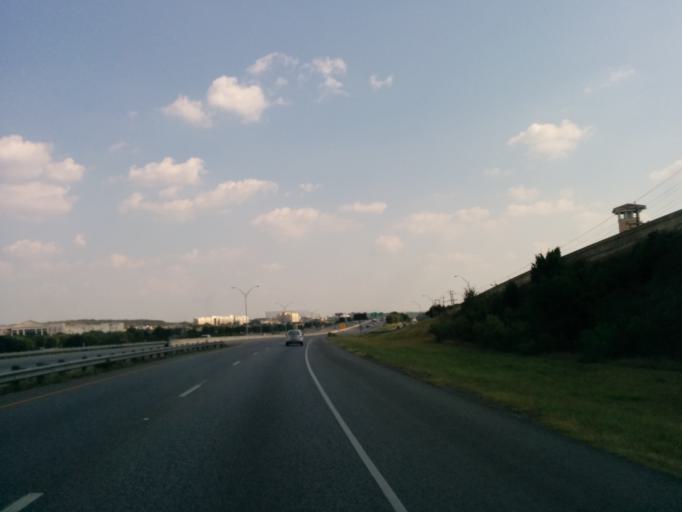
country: US
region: Texas
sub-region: Bexar County
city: Shavano Park
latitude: 29.6128
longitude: -98.6048
